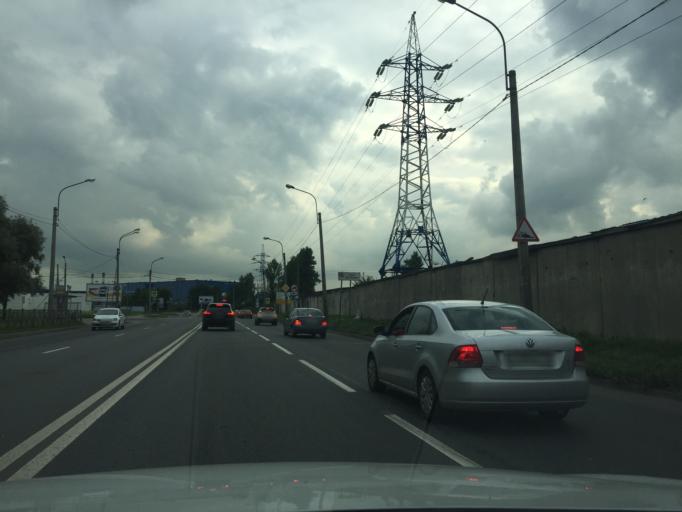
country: RU
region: St.-Petersburg
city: Avtovo
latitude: 59.8491
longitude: 30.2920
